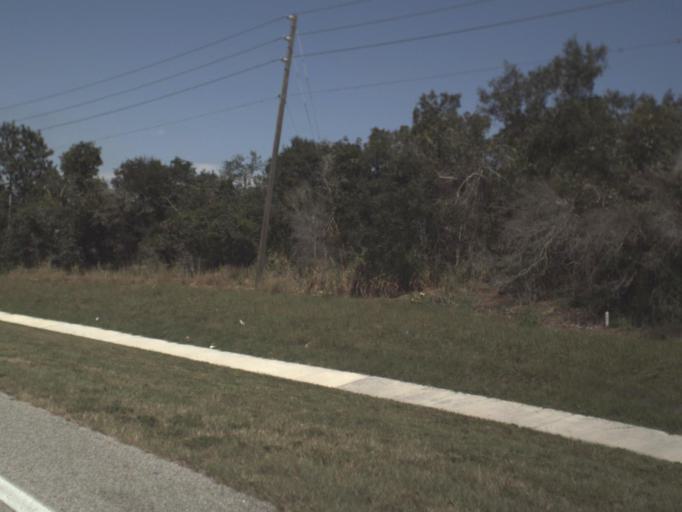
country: US
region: Florida
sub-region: Highlands County
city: Lake Placid
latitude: 27.3123
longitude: -81.3588
